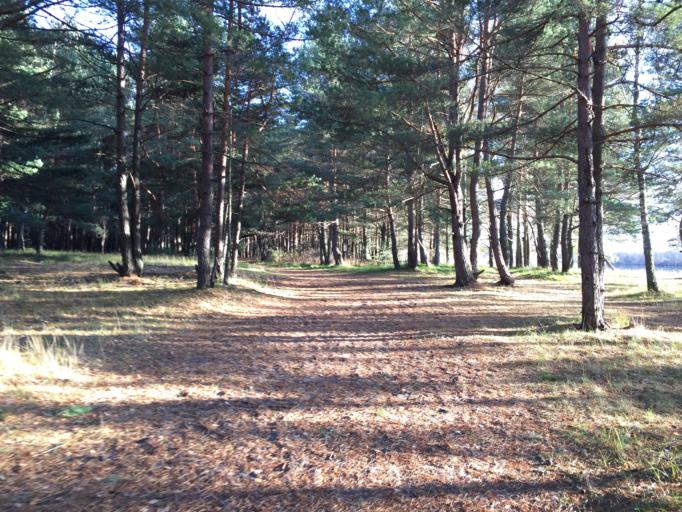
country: LV
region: Carnikava
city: Carnikava
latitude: 57.1560
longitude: 24.2743
